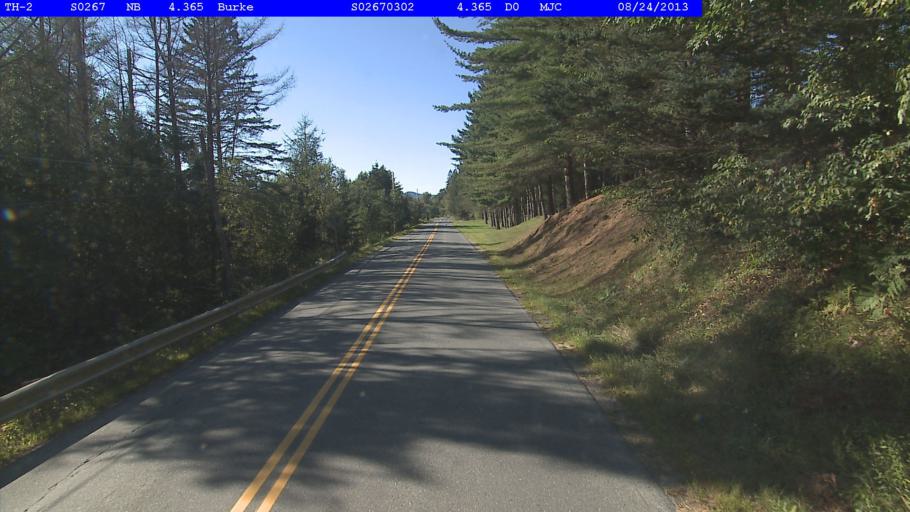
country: US
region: Vermont
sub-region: Caledonia County
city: Lyndonville
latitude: 44.6363
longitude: -71.9719
